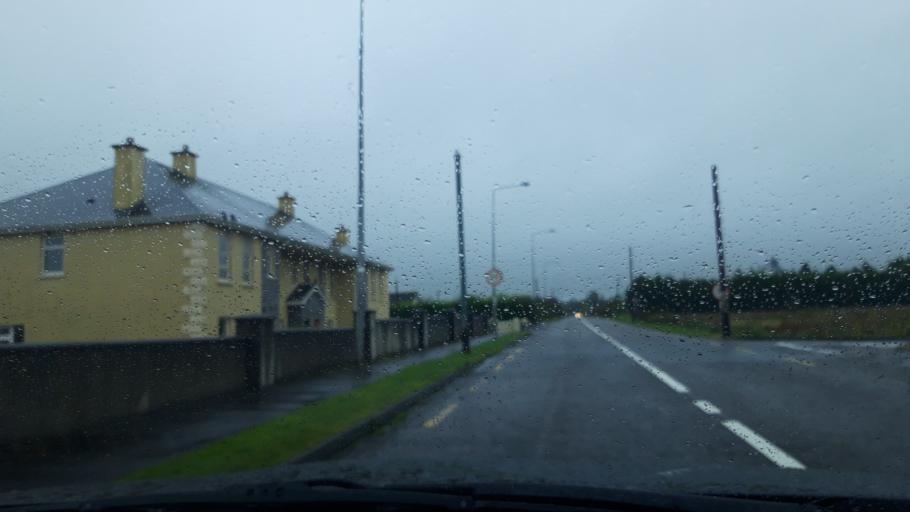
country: IE
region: Connaught
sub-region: Roscommon
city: Ballaghaderreen
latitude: 53.9064
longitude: -8.5891
